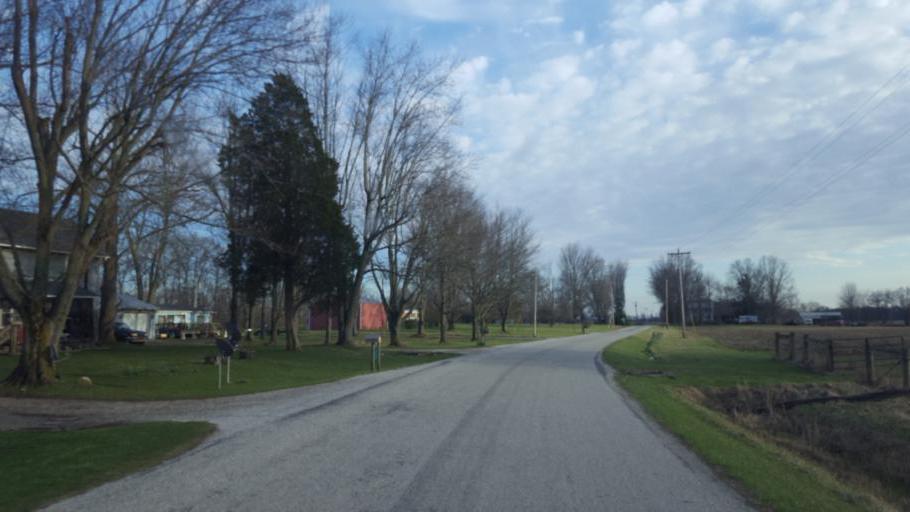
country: US
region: Ohio
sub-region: Crawford County
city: Bucyrus
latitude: 40.6593
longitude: -82.9484
